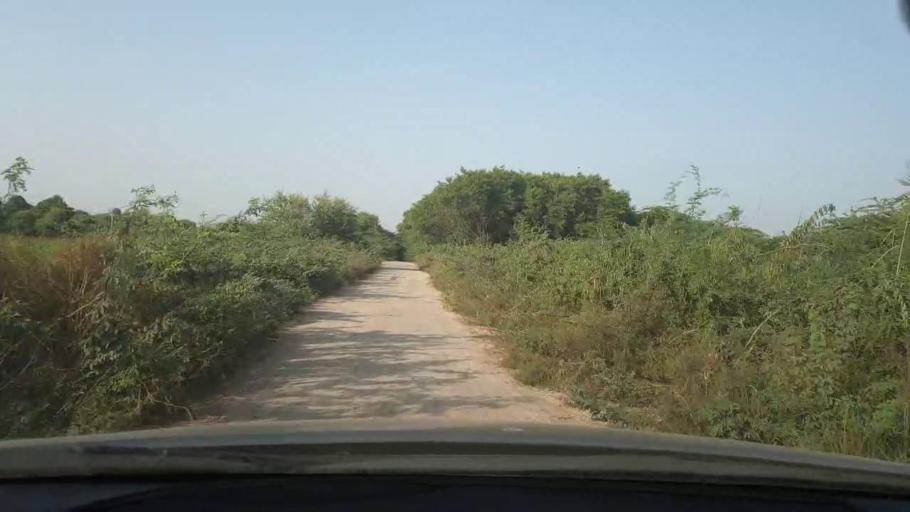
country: PK
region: Sindh
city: Naukot
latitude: 24.7843
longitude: 69.2353
